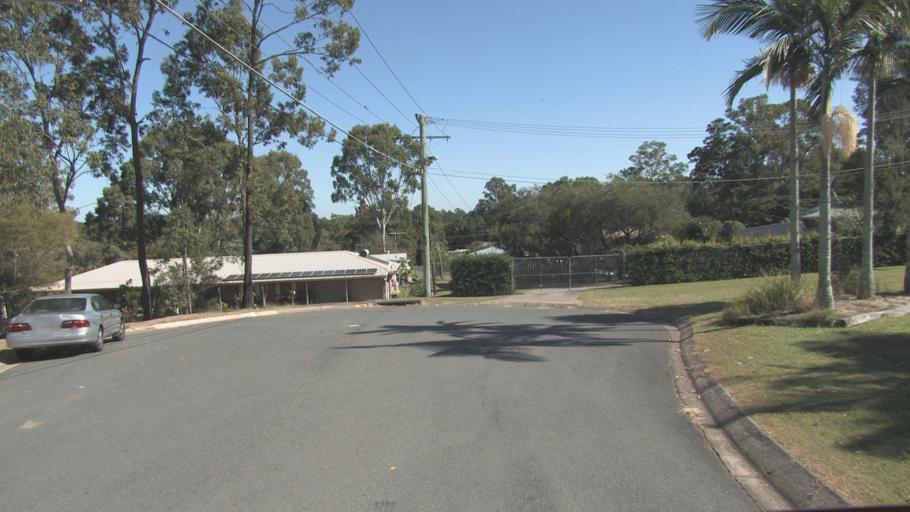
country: AU
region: Queensland
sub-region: Logan
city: Beenleigh
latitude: -27.6979
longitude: 153.2017
